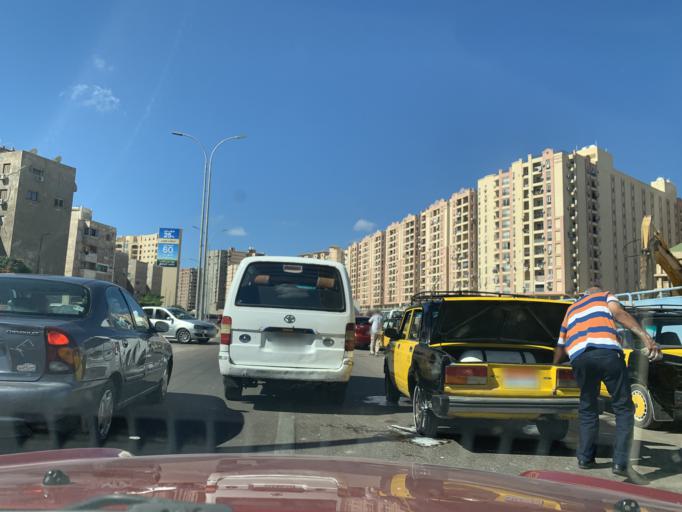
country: EG
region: Alexandria
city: Alexandria
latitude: 31.2146
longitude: 29.9614
